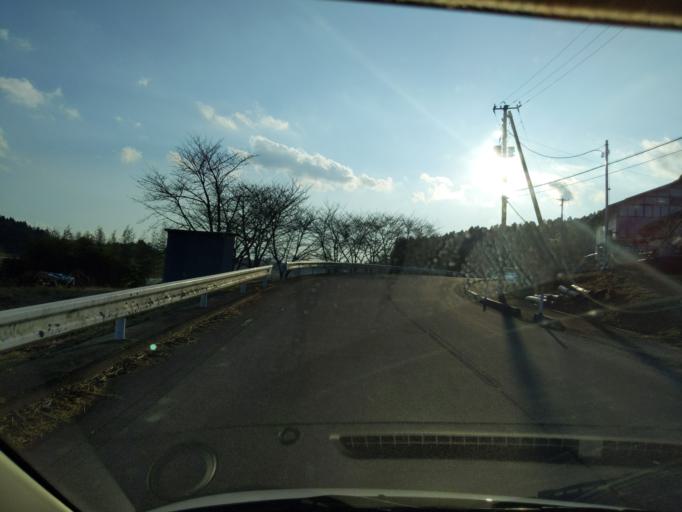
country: JP
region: Miyagi
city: Wakuya
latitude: 38.6835
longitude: 141.1134
